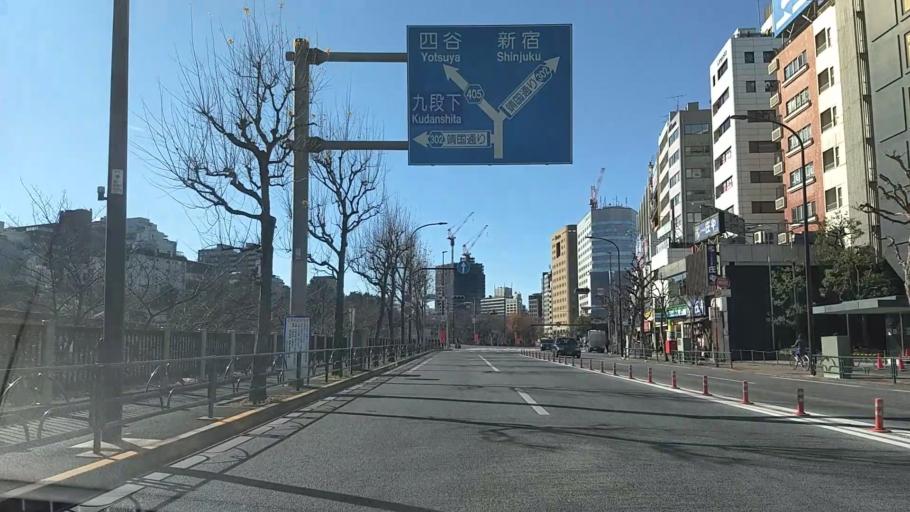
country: JP
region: Tokyo
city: Tokyo
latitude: 35.6931
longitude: 139.7365
